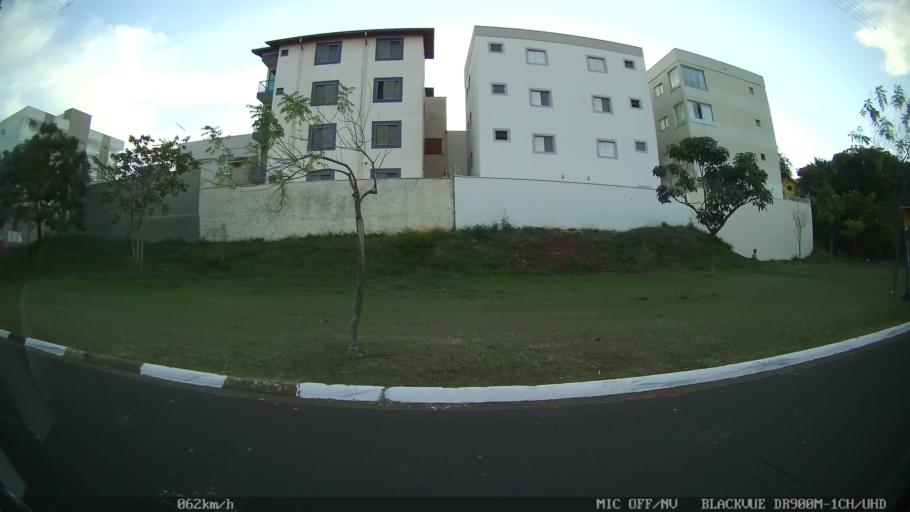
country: BR
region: Sao Paulo
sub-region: Franca
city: Franca
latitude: -20.5385
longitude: -47.4079
